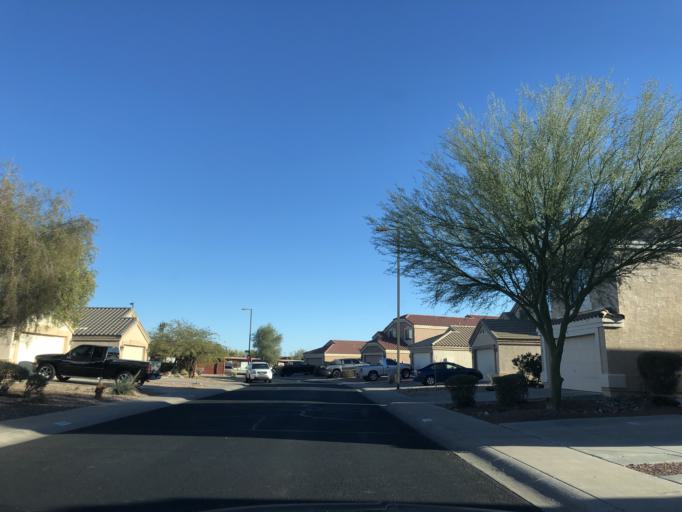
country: US
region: Arizona
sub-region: Maricopa County
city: Buckeye
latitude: 33.4389
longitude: -112.5649
